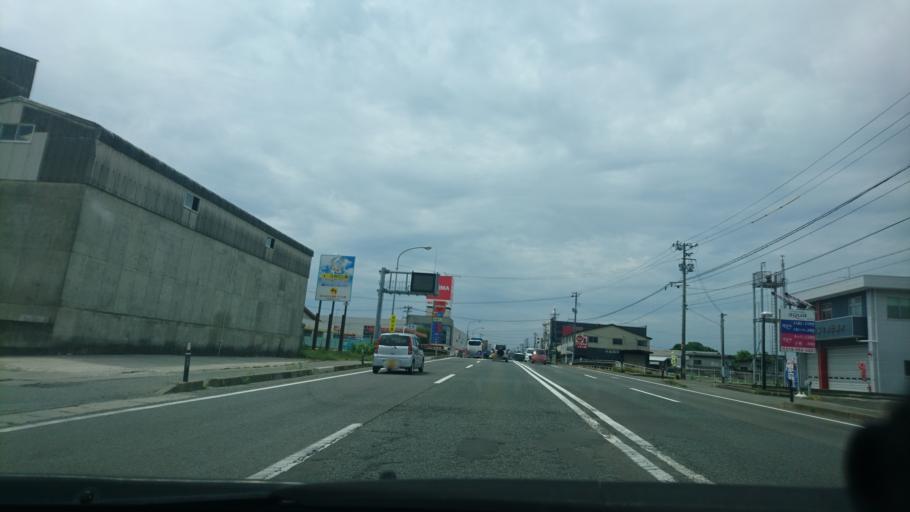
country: JP
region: Akita
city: Akita
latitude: 39.6992
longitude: 140.1140
